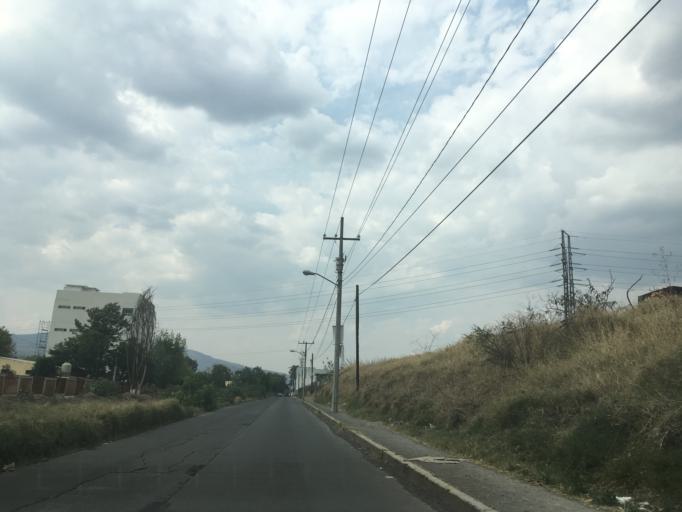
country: MX
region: Michoacan
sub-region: Morelia
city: Morelos
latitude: 19.6780
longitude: -101.2355
